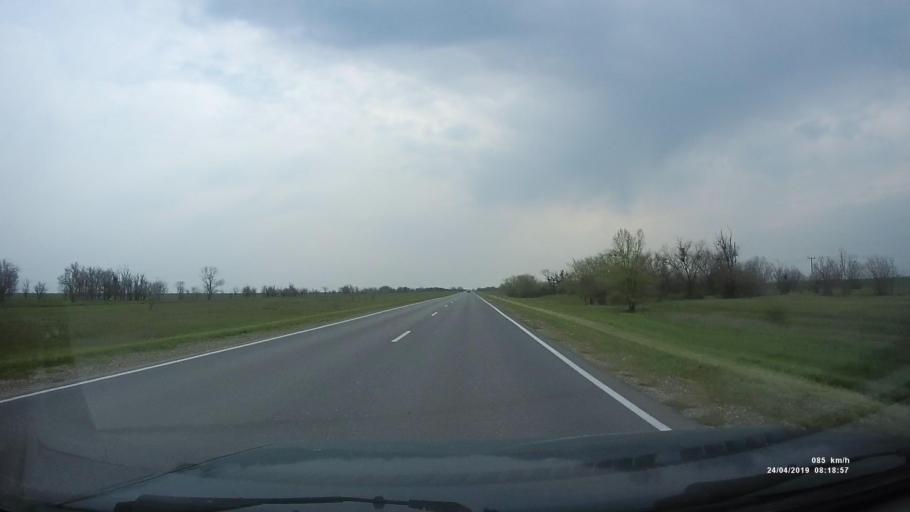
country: RU
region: Kalmykiya
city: Priyutnoye
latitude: 46.1020
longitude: 43.6557
